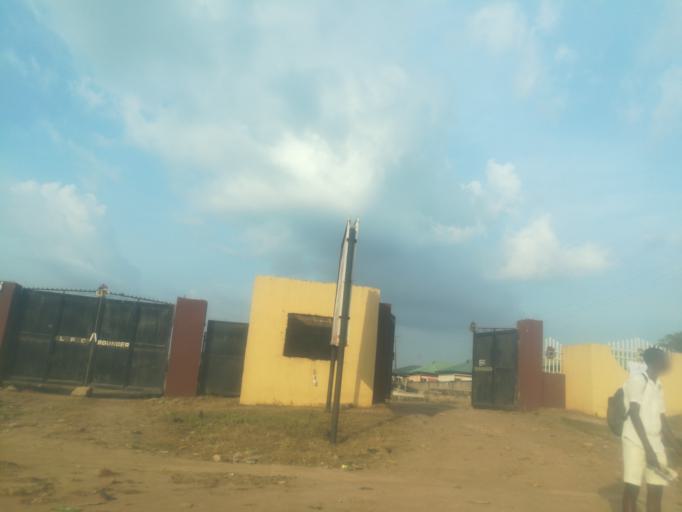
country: NG
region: Ogun
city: Abeokuta
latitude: 7.1704
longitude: 3.2947
